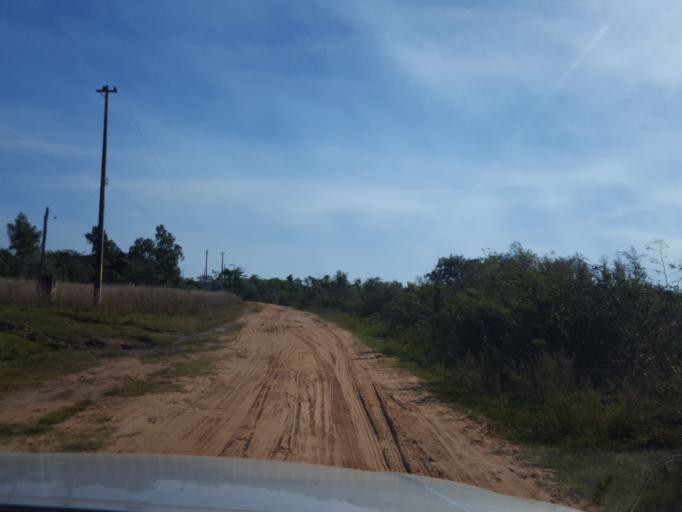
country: PY
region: Cordillera
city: Atyra
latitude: -25.2456
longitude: -57.1279
